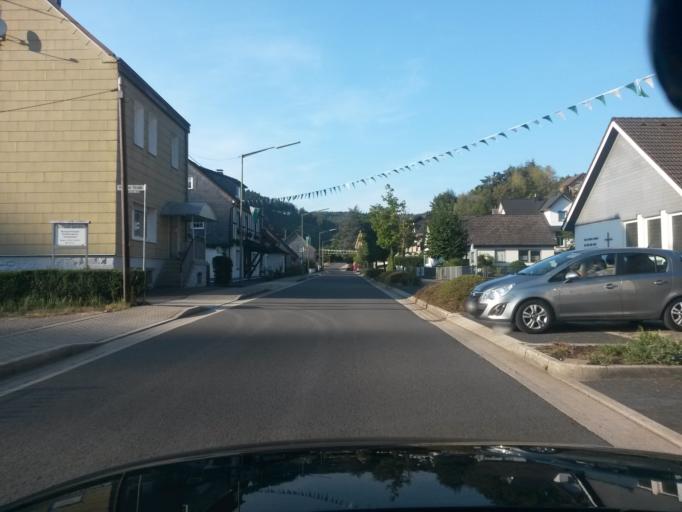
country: DE
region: North Rhine-Westphalia
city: Bergneustadt
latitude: 51.0257
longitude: 7.6152
